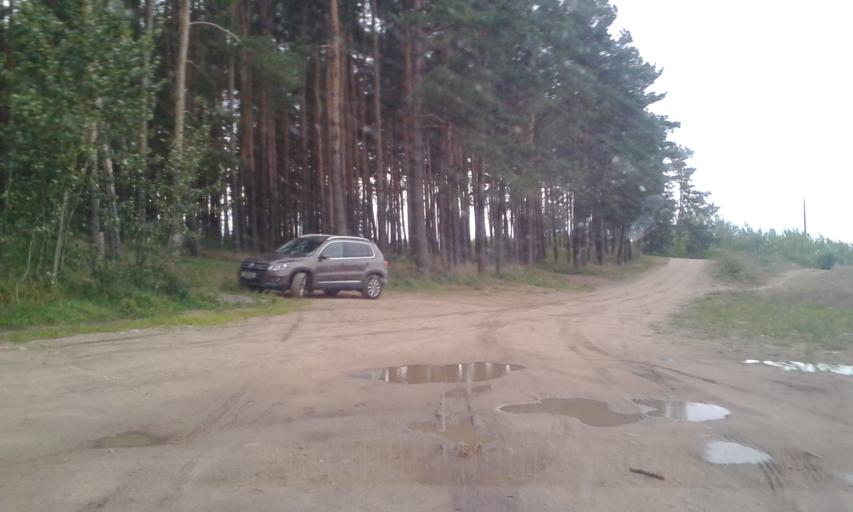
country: BY
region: Minsk
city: Minsk
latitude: 53.9498
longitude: 27.5688
